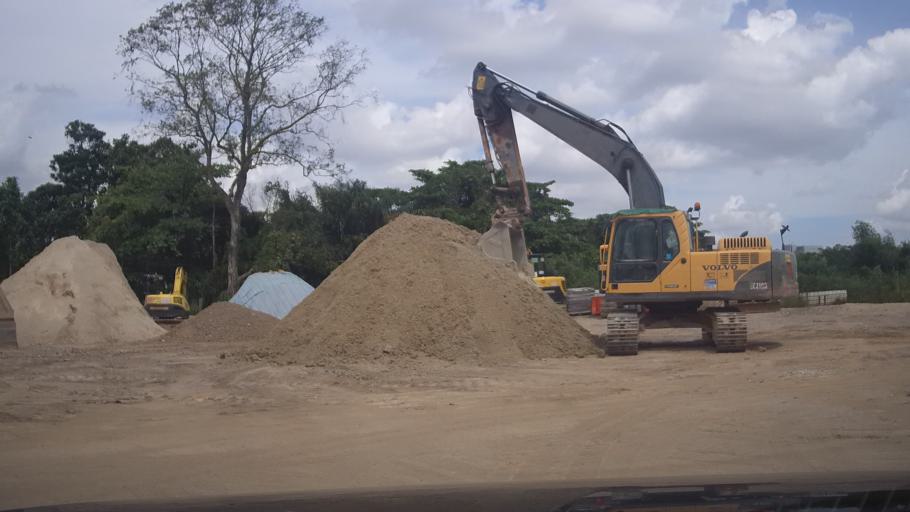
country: MY
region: Johor
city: Kampung Pasir Gudang Baru
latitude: 1.3995
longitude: 103.8629
